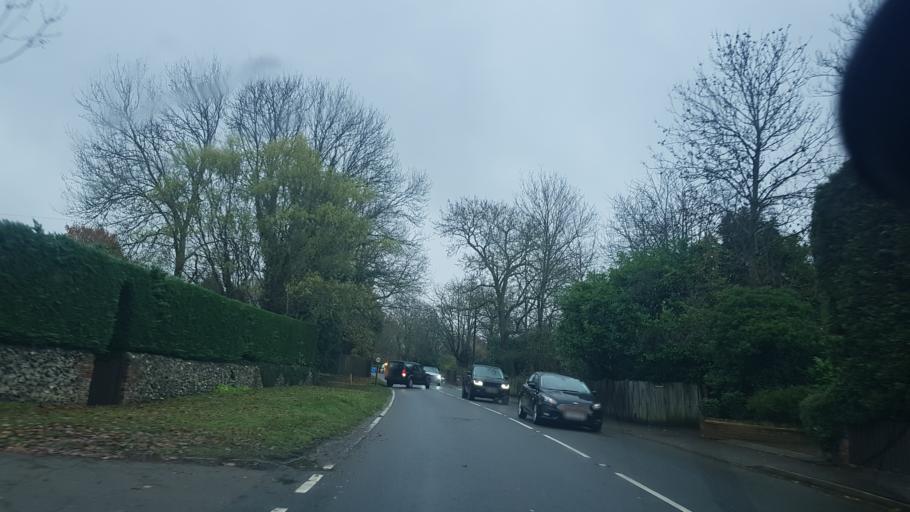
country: GB
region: England
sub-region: Surrey
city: Send
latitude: 51.2631
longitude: -0.5045
